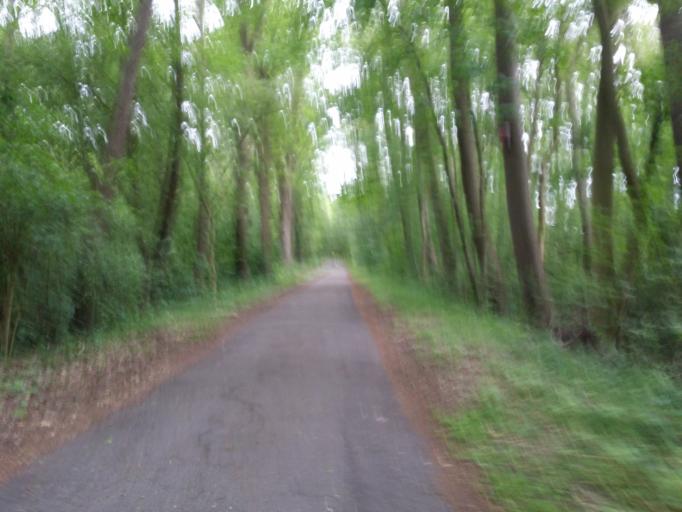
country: DE
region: Lower Saxony
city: Oldenburg
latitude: 53.1497
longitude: 8.2798
